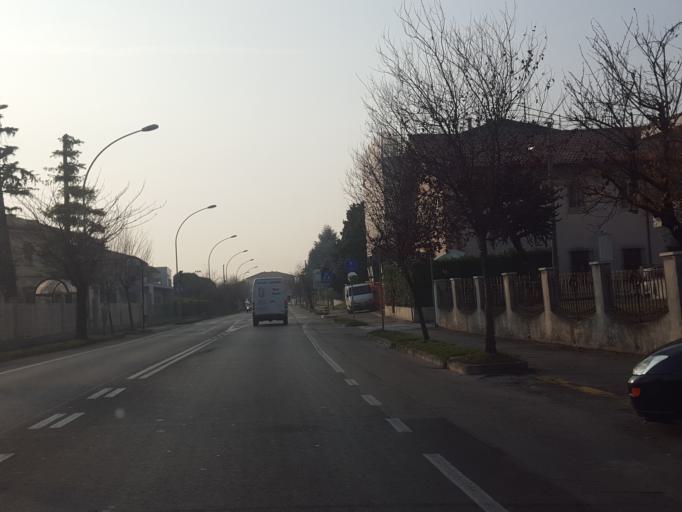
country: IT
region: Veneto
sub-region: Provincia di Treviso
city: Treviso
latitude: 45.6591
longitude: 12.2162
